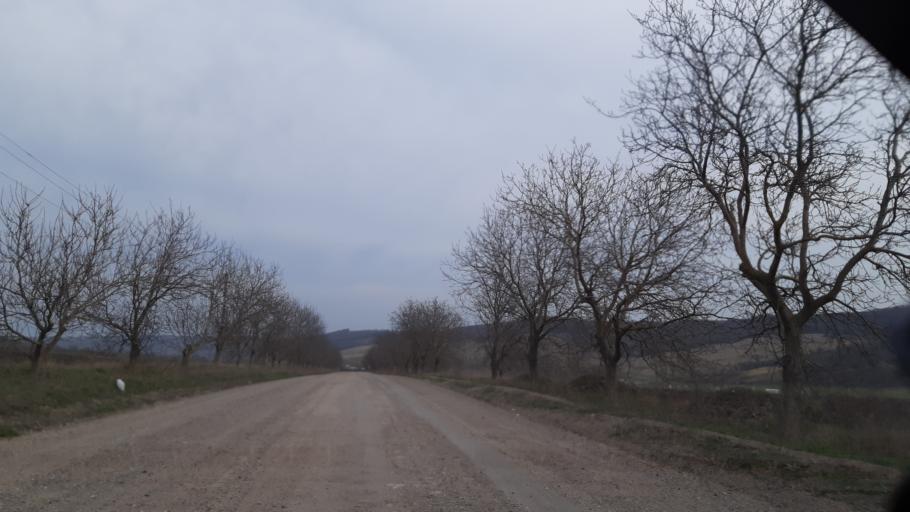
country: MD
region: Soldanesti
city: Soldanesti
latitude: 47.6913
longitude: 28.7395
